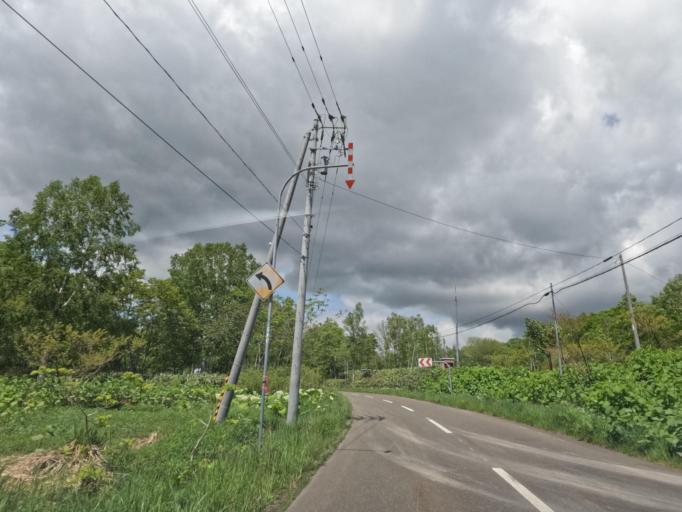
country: JP
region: Hokkaido
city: Tobetsu
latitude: 43.4429
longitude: 141.5839
